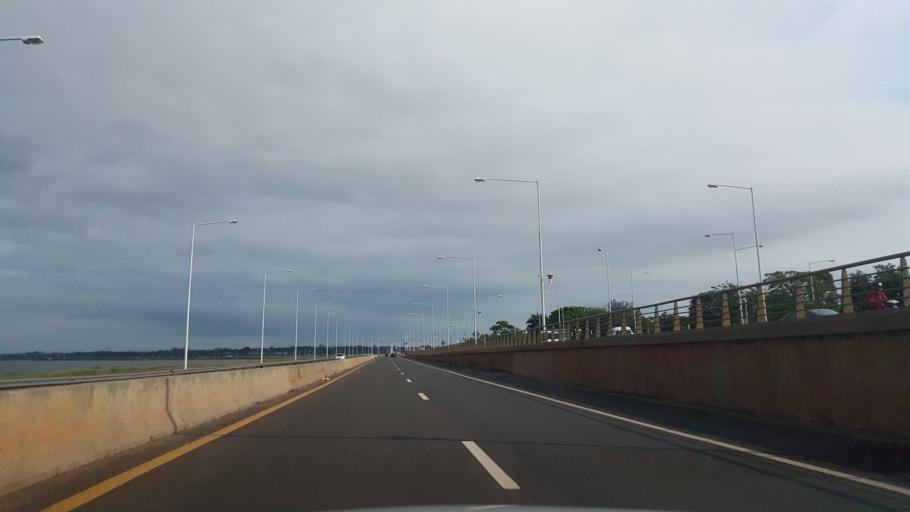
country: AR
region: Misiones
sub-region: Departamento de Capital
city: Posadas
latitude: -27.3987
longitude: -55.8924
